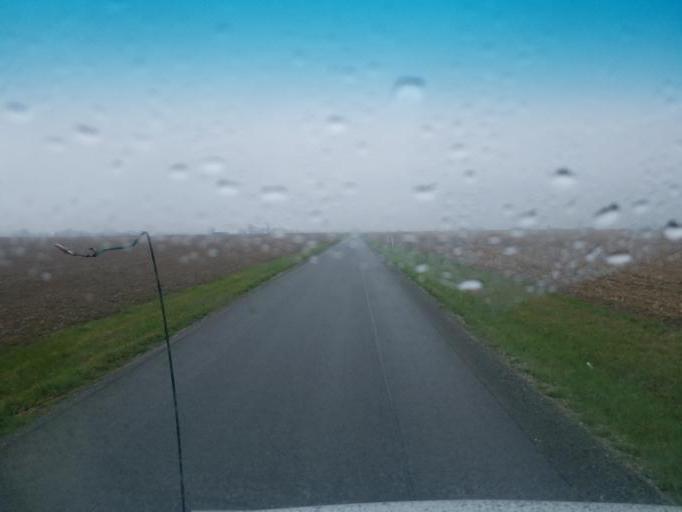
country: US
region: Ohio
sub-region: Wyandot County
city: Carey
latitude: 40.9924
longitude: -83.3347
